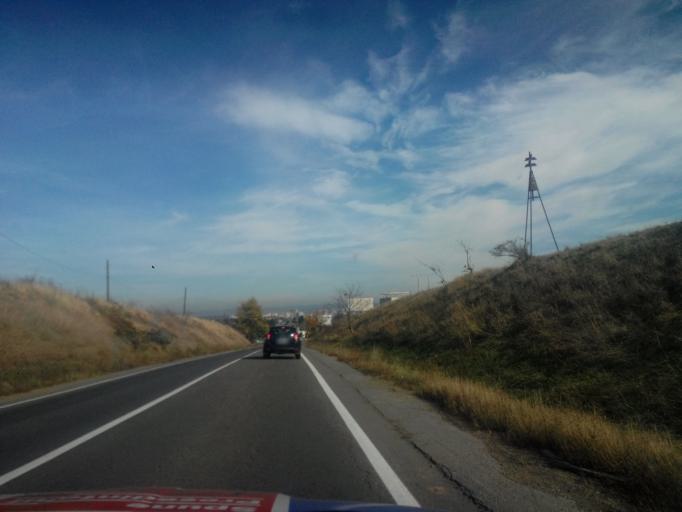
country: RO
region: Bacau
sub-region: Municipiul Bacau
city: Bacau
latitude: 46.5551
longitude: 26.8822
